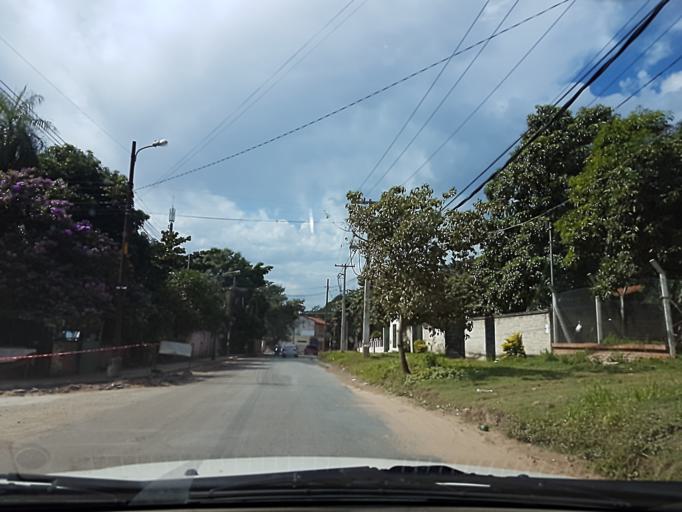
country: PY
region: Central
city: Colonia Mariano Roque Alonso
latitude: -25.2345
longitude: -57.5747
